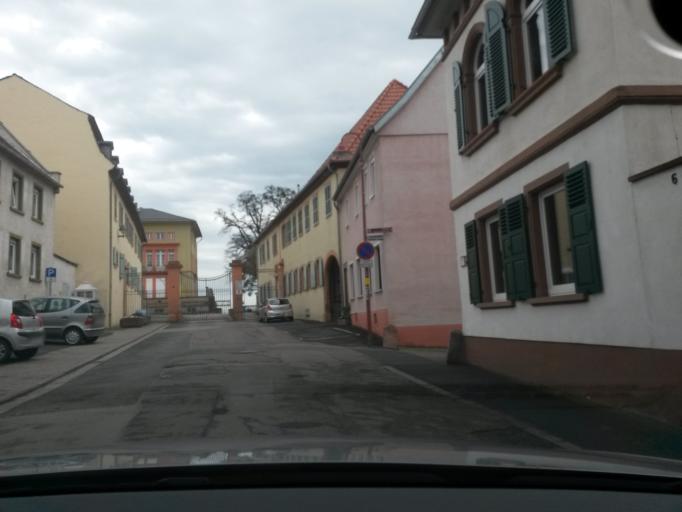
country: DE
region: Rheinland-Pfalz
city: Worms
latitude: 49.6585
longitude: 8.3301
